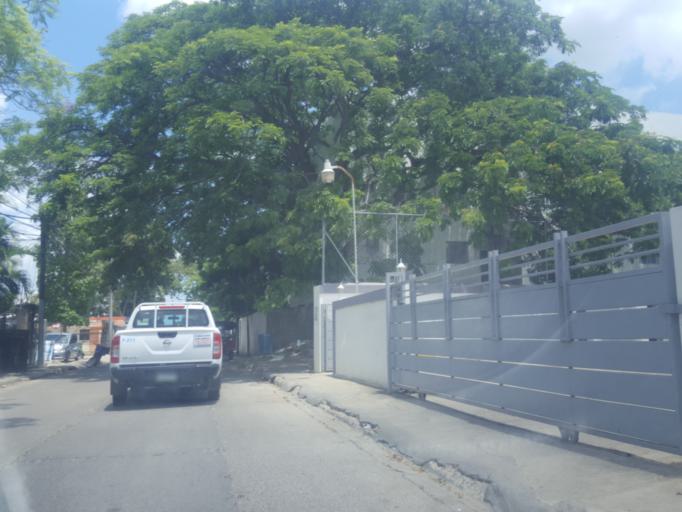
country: DO
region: Santiago
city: Santiago de los Caballeros
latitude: 19.4716
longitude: -70.6652
